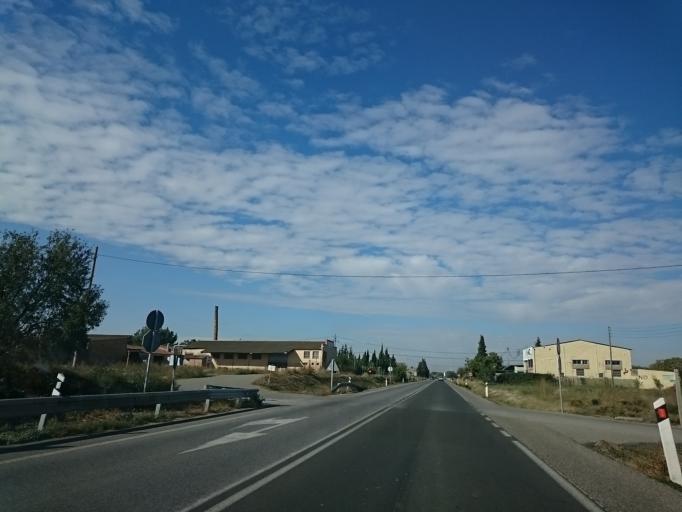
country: ES
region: Catalonia
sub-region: Provincia de Lleida
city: Juneda
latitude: 41.5406
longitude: 0.8277
